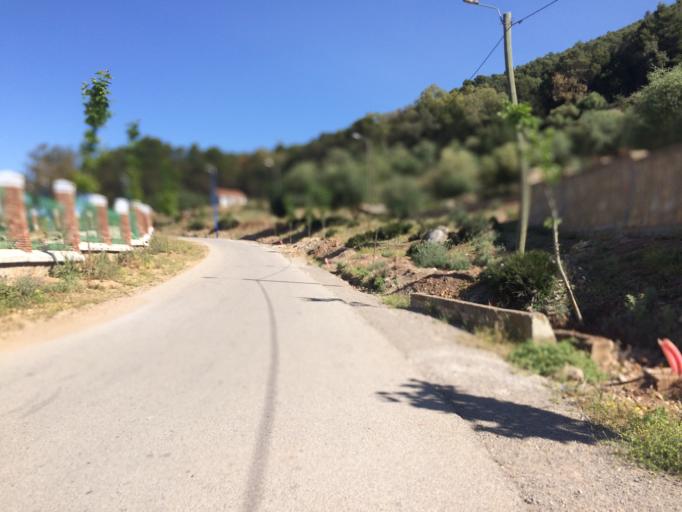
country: MA
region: Tanger-Tetouan
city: Chefchaouene
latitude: 35.1730
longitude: -5.2619
